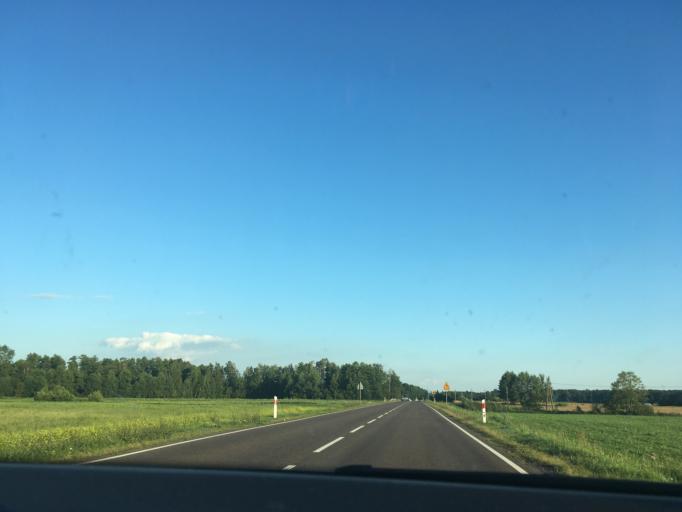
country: PL
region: Lublin Voivodeship
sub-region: Powiat bialski
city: Miedzyrzec Podlaski
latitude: 52.0674
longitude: 22.7327
